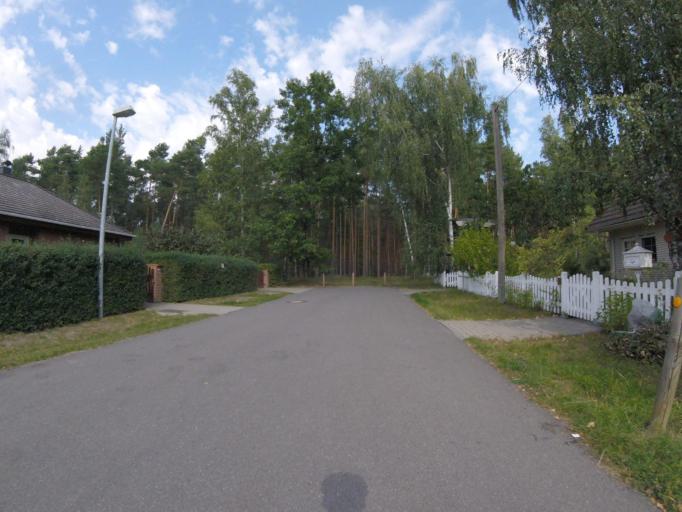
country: DE
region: Brandenburg
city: Bestensee
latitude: 52.2788
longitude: 13.6603
